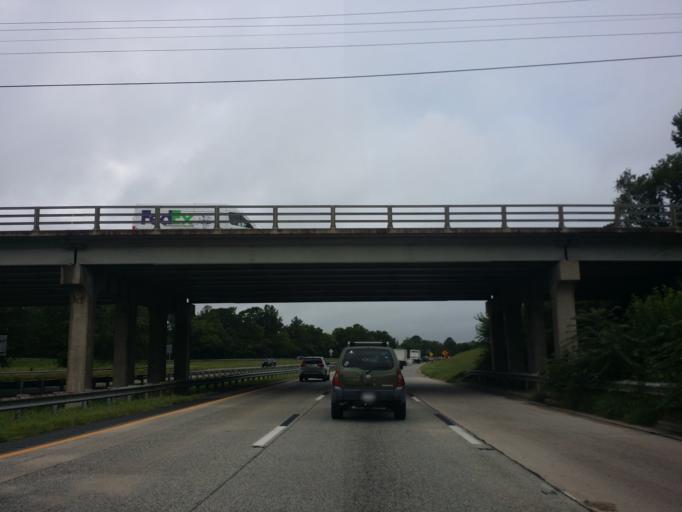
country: US
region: North Carolina
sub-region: Durham County
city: Durham
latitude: 35.9822
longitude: -78.8900
